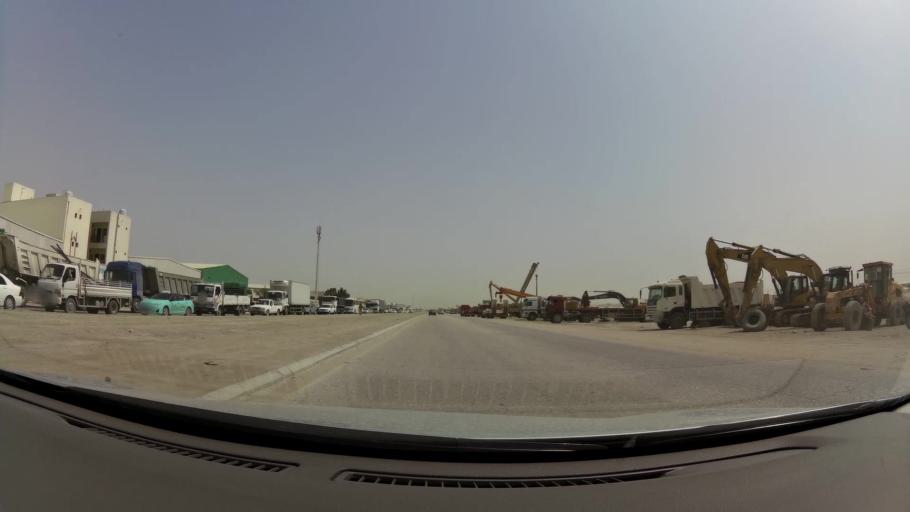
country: QA
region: Baladiyat ar Rayyan
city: Ar Rayyan
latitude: 25.1839
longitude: 51.4285
